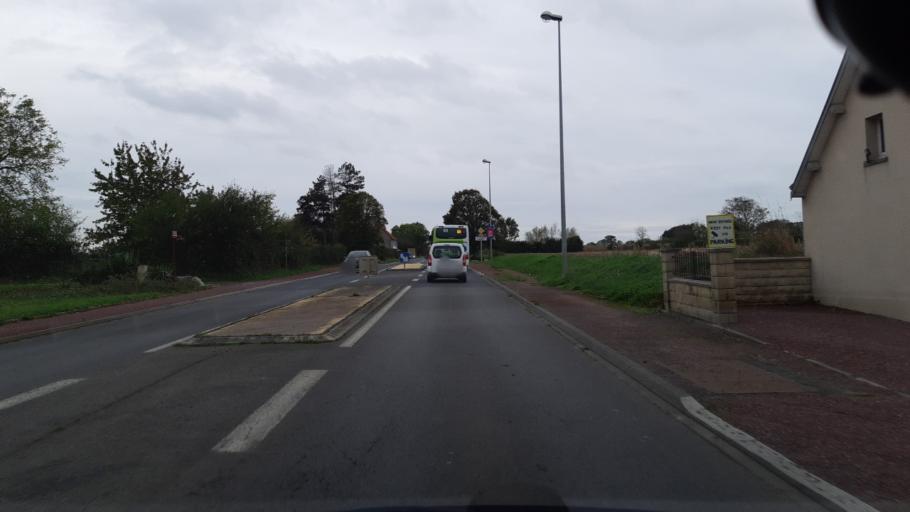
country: FR
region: Lower Normandy
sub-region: Departement de la Manche
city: Brehal
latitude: 48.8810
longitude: -1.5306
